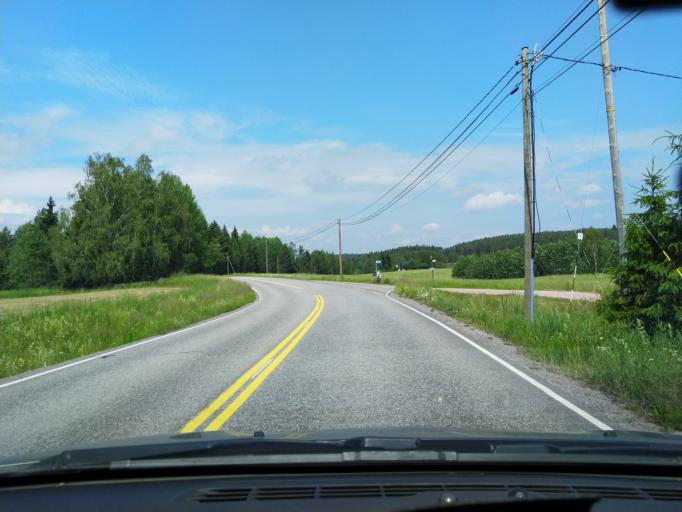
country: FI
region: Uusimaa
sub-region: Helsinki
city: Lohja
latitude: 60.3180
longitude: 24.0770
